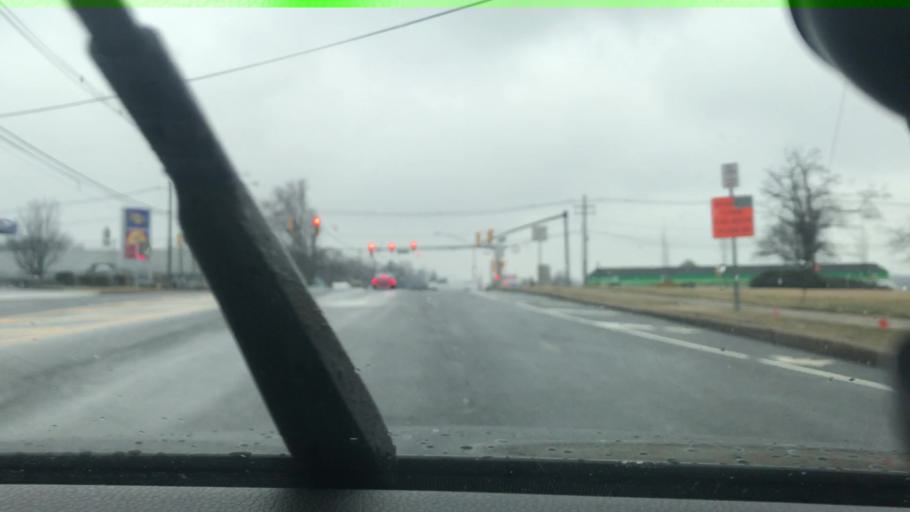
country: US
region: New Jersey
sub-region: Morris County
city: Morristown
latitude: 40.8069
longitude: -74.4612
